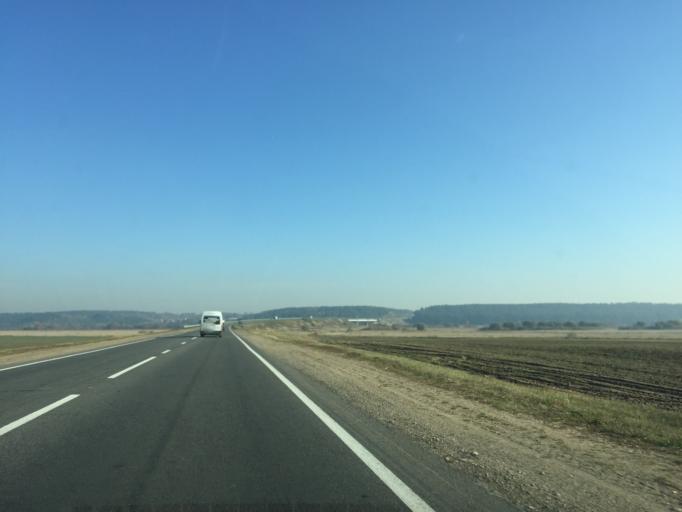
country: BY
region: Mogilev
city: Palykavichy Pyershyya
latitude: 53.9769
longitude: 30.3810
